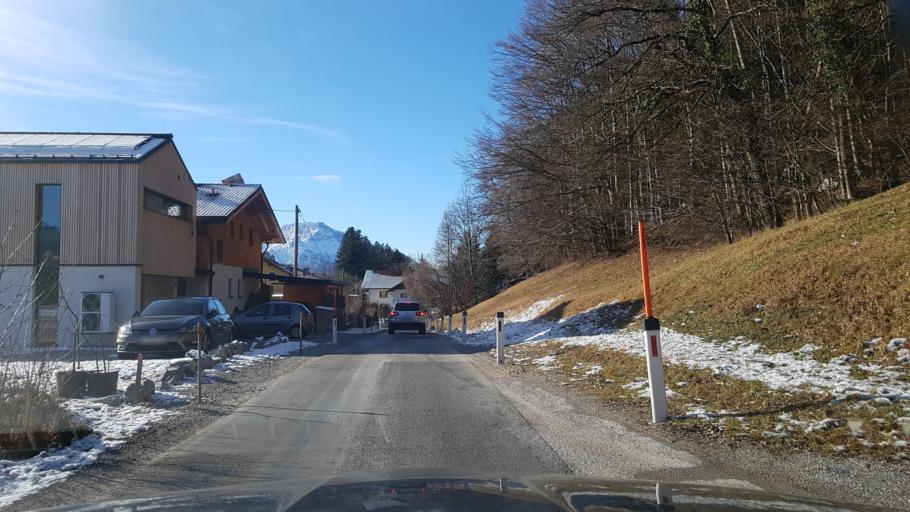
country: AT
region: Salzburg
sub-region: Politischer Bezirk Salzburg-Umgebung
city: Koppl
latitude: 47.7754
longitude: 13.1327
